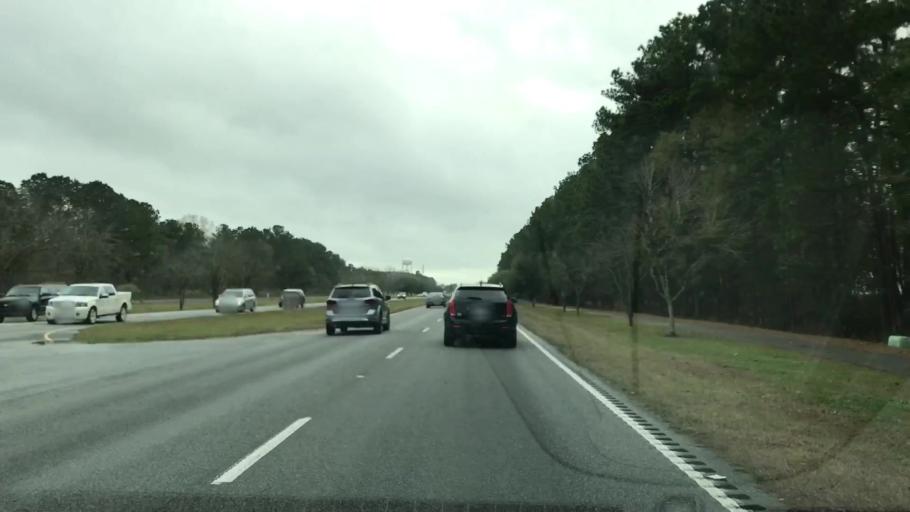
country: US
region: South Carolina
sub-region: Berkeley County
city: Goose Creek
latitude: 33.0159
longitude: -80.0365
